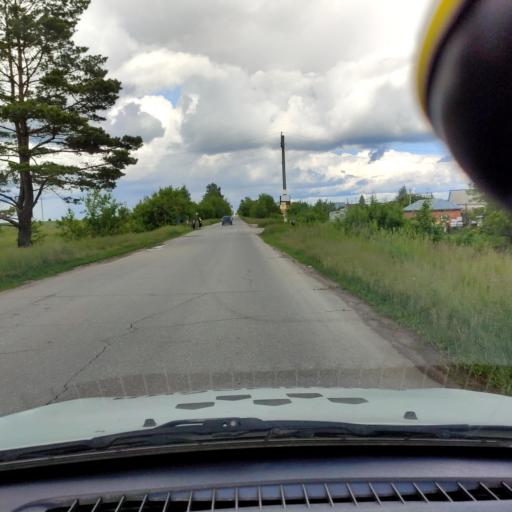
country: RU
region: Samara
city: Povolzhskiy
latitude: 53.6457
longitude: 49.7837
